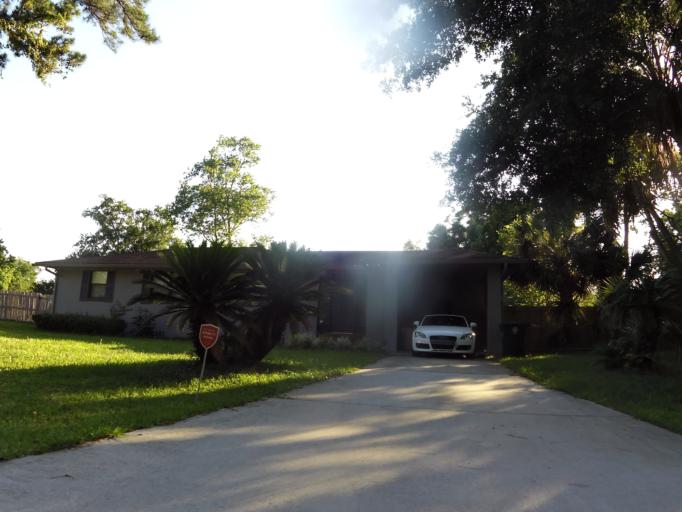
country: US
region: Florida
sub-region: Duval County
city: Jacksonville
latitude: 30.2373
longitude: -81.6168
